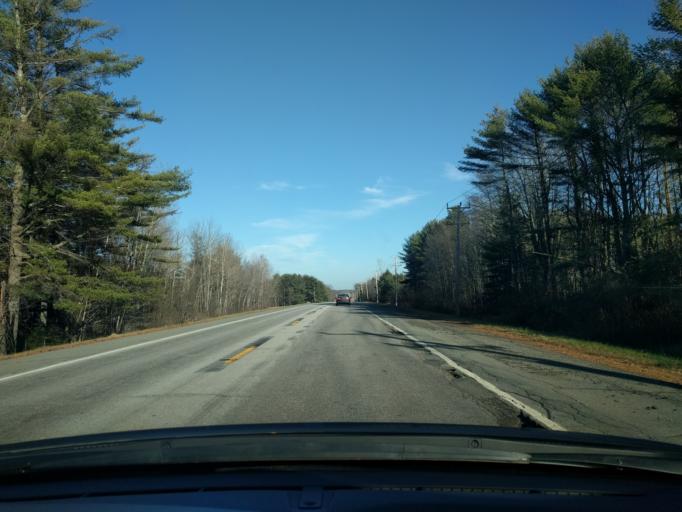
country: US
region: Maine
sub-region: Penobscot County
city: Hampden
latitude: 44.7673
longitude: -68.8141
